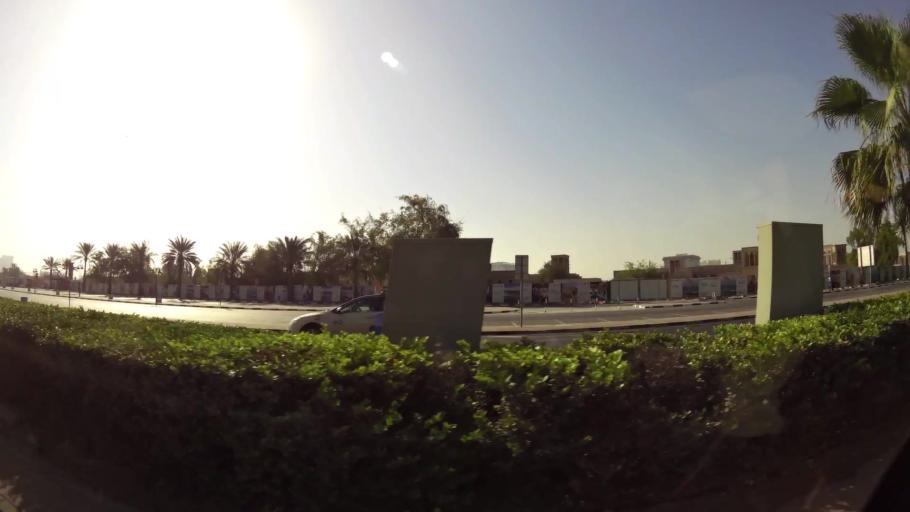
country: AE
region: Ash Shariqah
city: Sharjah
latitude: 25.2692
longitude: 55.2892
